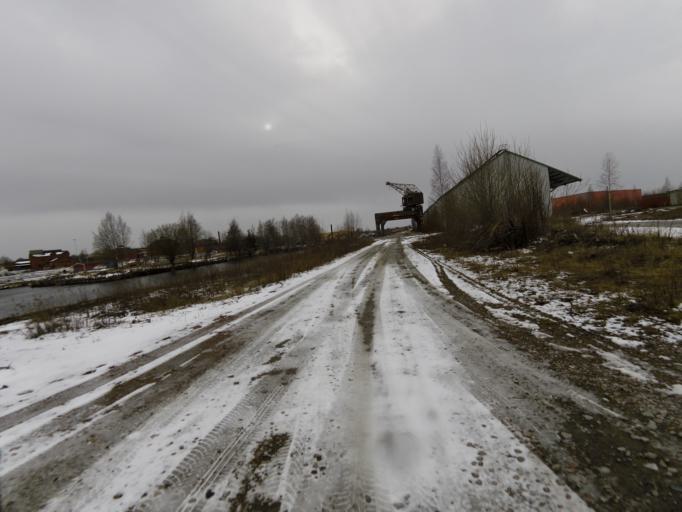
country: SE
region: Gaevleborg
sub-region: Gavle Kommun
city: Gavle
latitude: 60.6811
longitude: 17.1821
